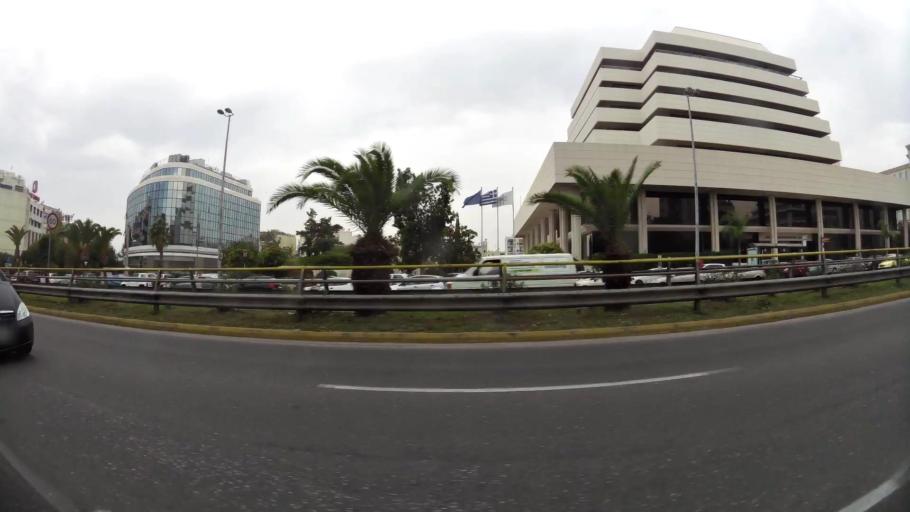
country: GR
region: Attica
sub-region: Nomarchia Athinas
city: Kallithea
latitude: 37.9420
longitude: 23.6979
